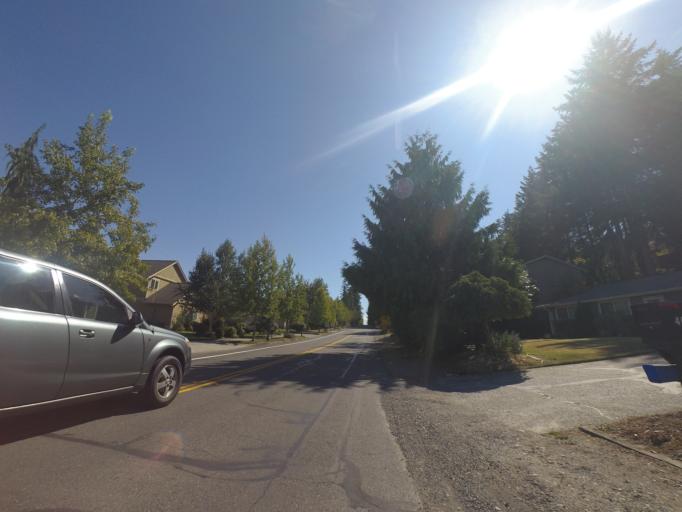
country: US
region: Washington
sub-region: Pierce County
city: Fircrest
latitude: 47.2149
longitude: -122.5160
